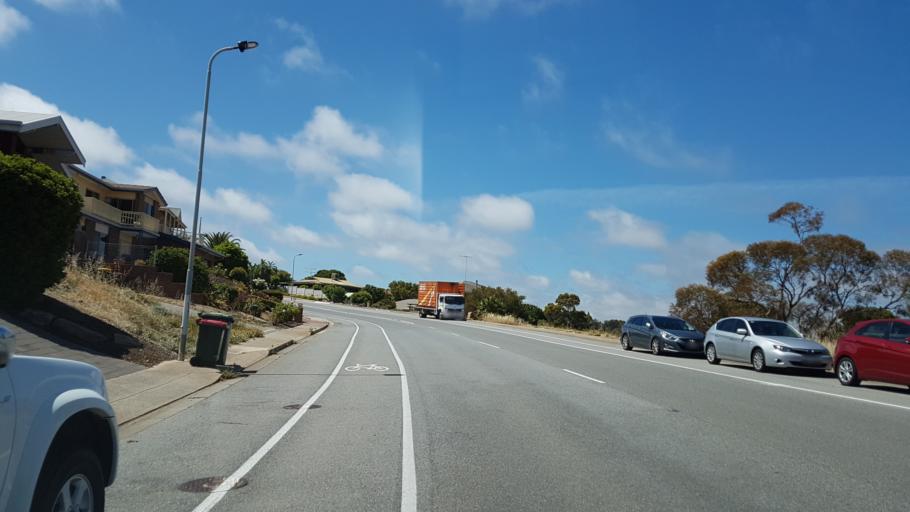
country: AU
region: South Australia
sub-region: Marion
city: Marino
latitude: -35.0688
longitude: 138.5066
